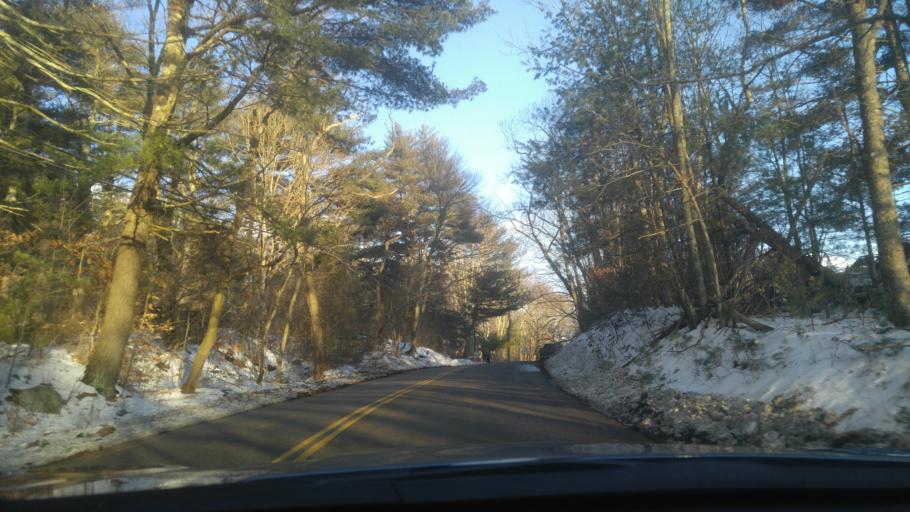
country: US
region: Rhode Island
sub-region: Kent County
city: Coventry
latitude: 41.7195
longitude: -71.6631
